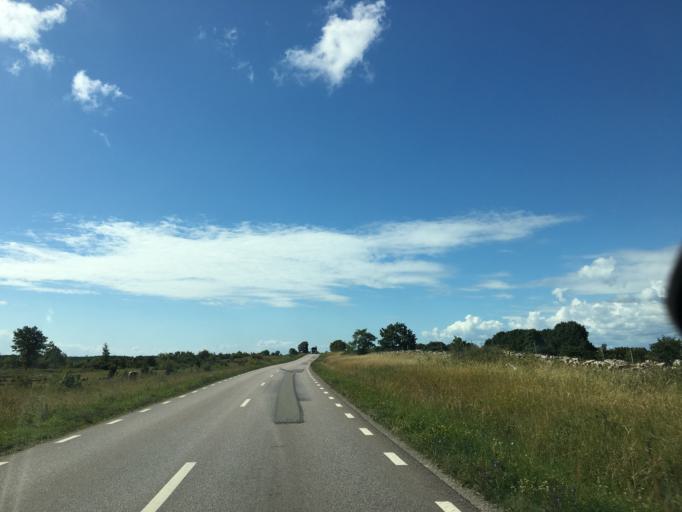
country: SE
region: Kalmar
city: Faerjestaden
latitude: 56.5705
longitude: 16.4565
